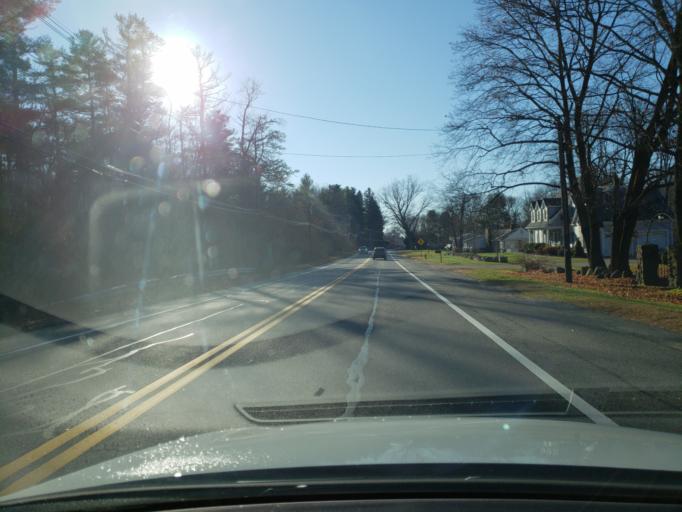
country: US
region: Massachusetts
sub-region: Essex County
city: Andover
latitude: 42.6334
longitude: -71.1284
